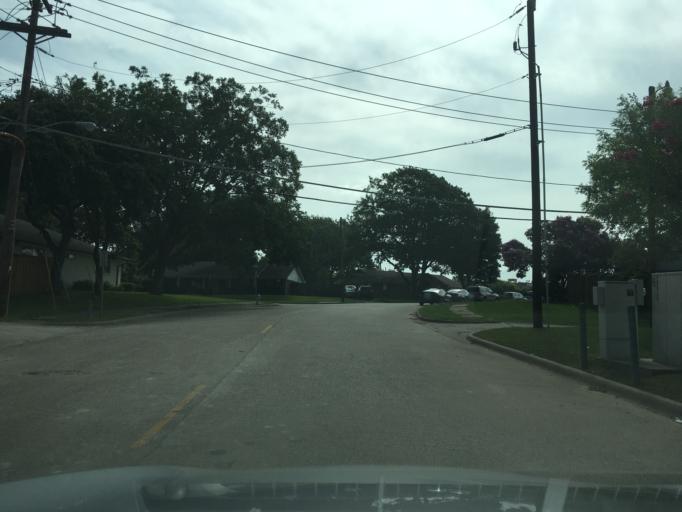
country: US
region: Texas
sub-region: Dallas County
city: Richardson
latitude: 32.9264
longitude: -96.7781
